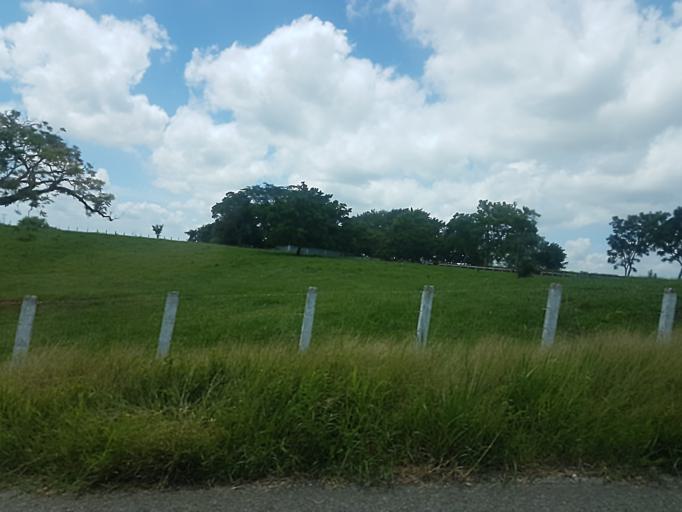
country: MX
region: Tabasco
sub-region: Jalapa
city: Aquiles Serdan 1ra. Seccion
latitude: 17.8138
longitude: -92.7140
